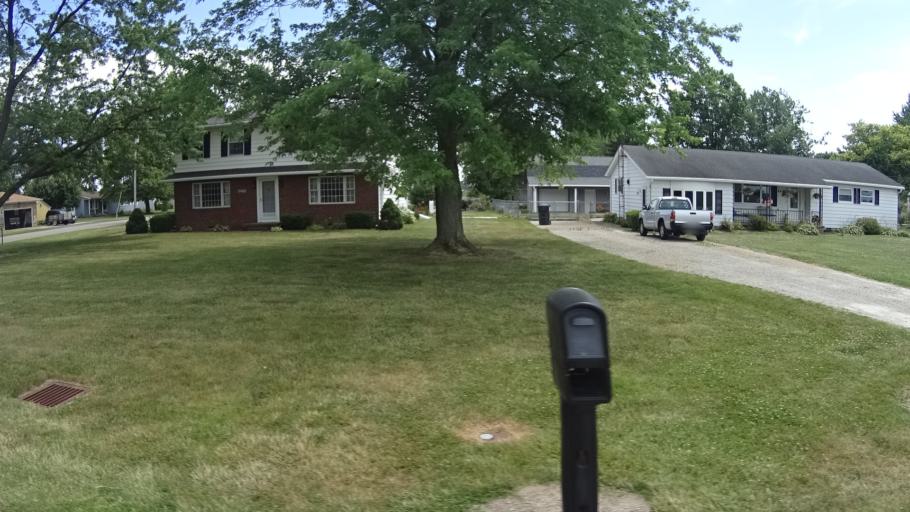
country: US
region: Ohio
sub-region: Erie County
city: Sandusky
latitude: 41.3981
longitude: -82.7807
